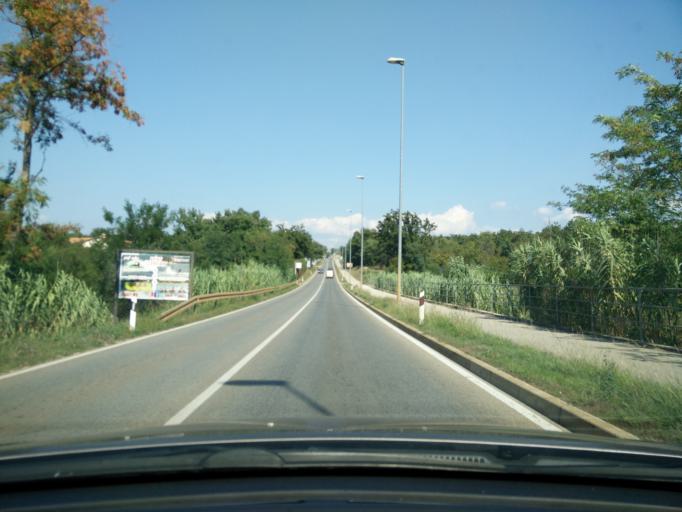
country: HR
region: Istarska
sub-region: Grad Porec
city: Porec
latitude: 45.2559
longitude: 13.6248
